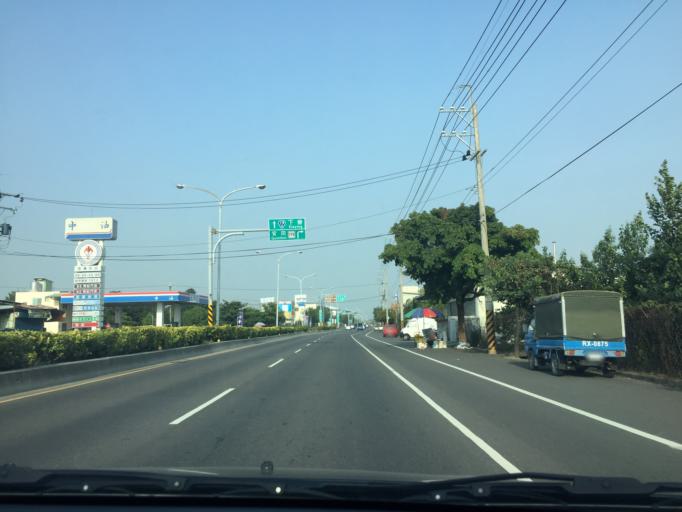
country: TW
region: Taiwan
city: Xinying
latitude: 23.1917
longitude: 120.2575
